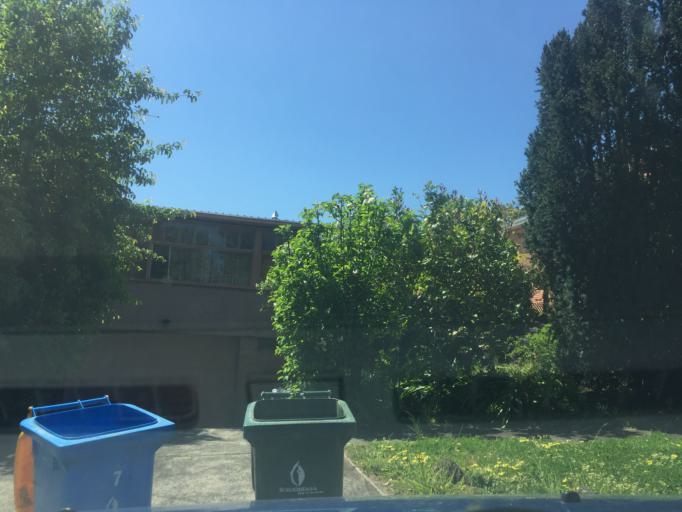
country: AU
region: Victoria
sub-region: Whitehorse
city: Surrey Hills
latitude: -37.8277
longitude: 145.0961
